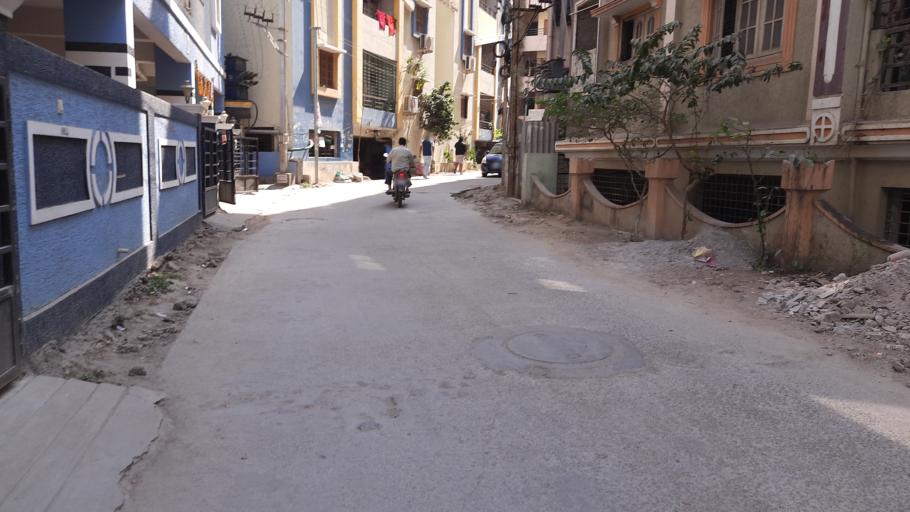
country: IN
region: Telangana
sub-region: Rangareddi
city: Kukatpalli
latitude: 17.5147
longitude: 78.3799
